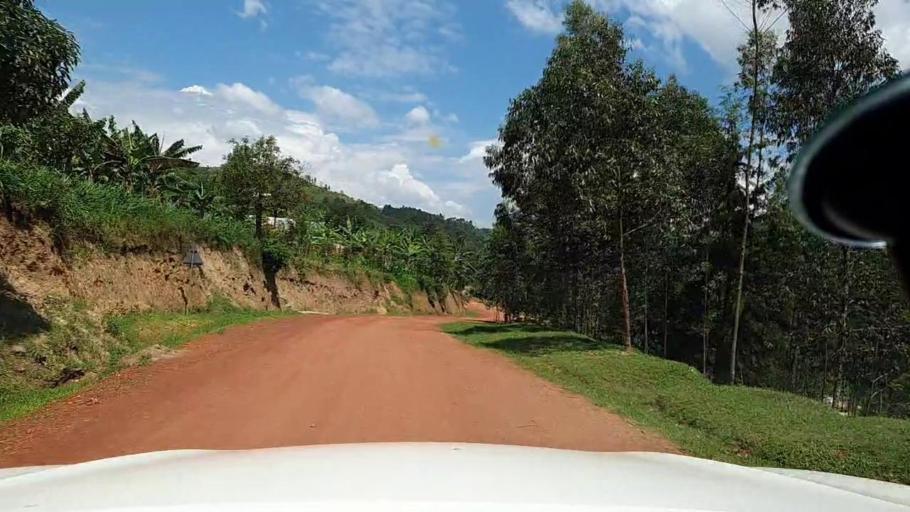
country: RW
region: Kigali
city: Kigali
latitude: -1.7747
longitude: 29.8747
